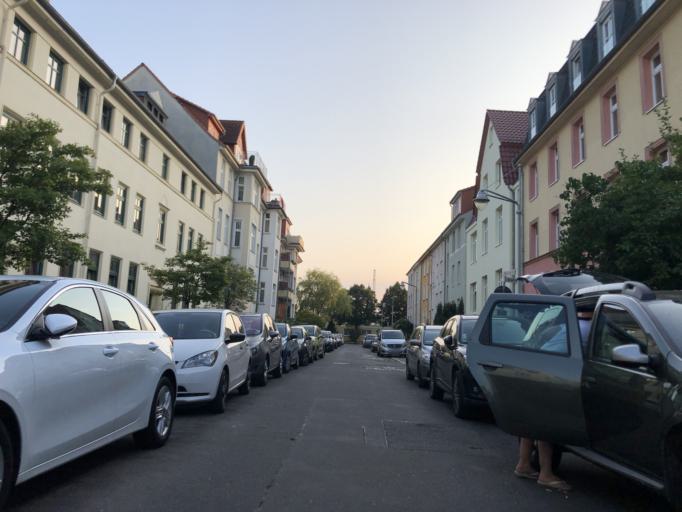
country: DE
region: Mecklenburg-Vorpommern
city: Rostock
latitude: 54.0764
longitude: 12.1381
